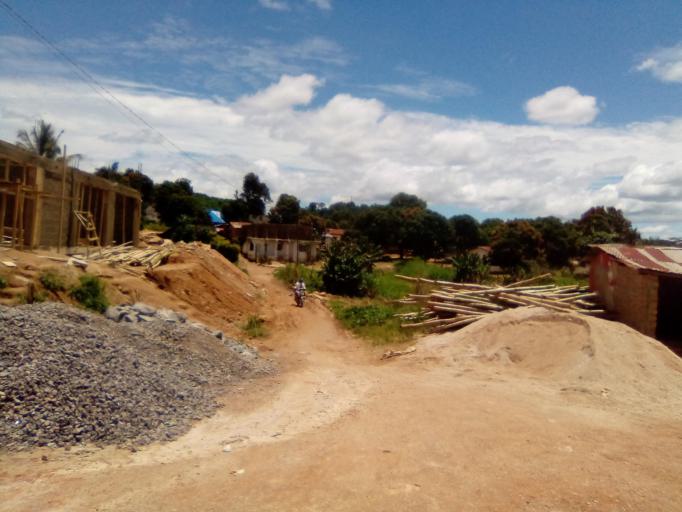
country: SL
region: Eastern Province
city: Koidu
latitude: 8.6341
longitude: -10.9839
